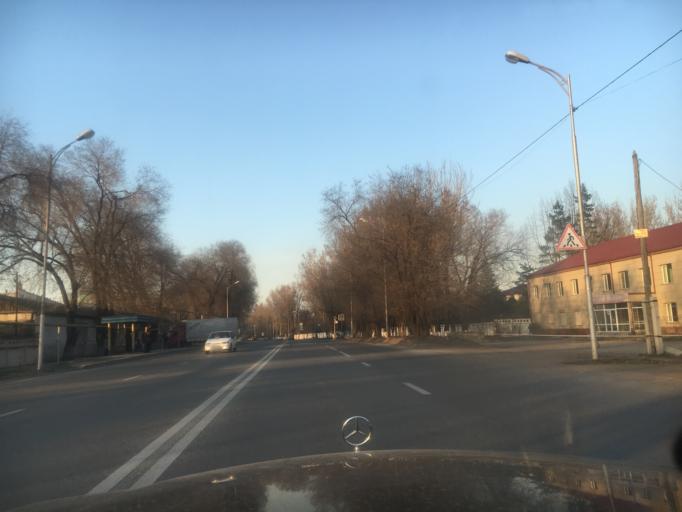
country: KZ
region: Almaty Oblysy
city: Pervomayskiy
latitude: 43.3655
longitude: 76.9853
